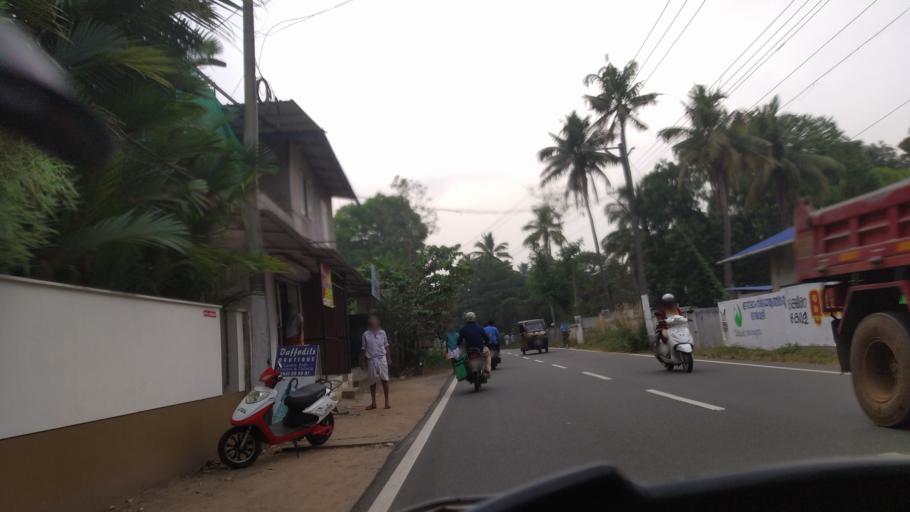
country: IN
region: Kerala
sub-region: Ernakulam
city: Elur
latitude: 10.1499
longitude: 76.2567
